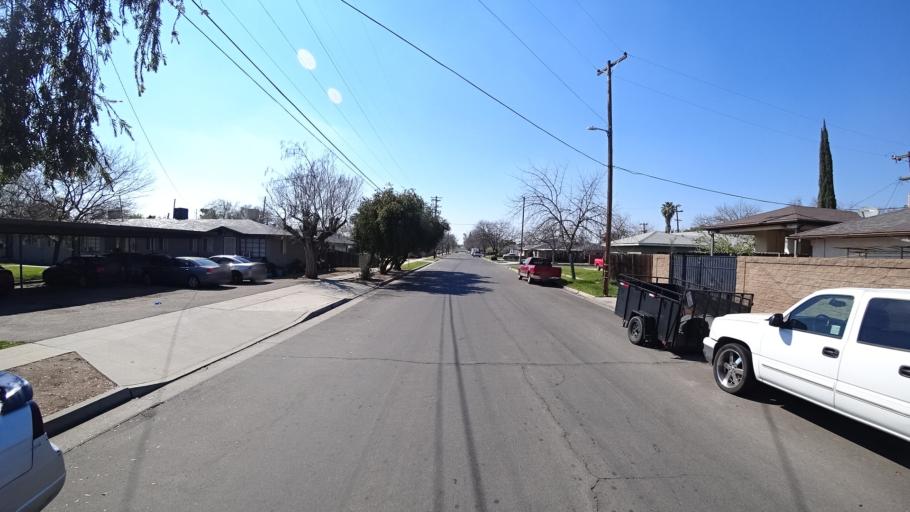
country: US
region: California
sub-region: Fresno County
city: Tarpey Village
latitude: 36.7977
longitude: -119.7366
